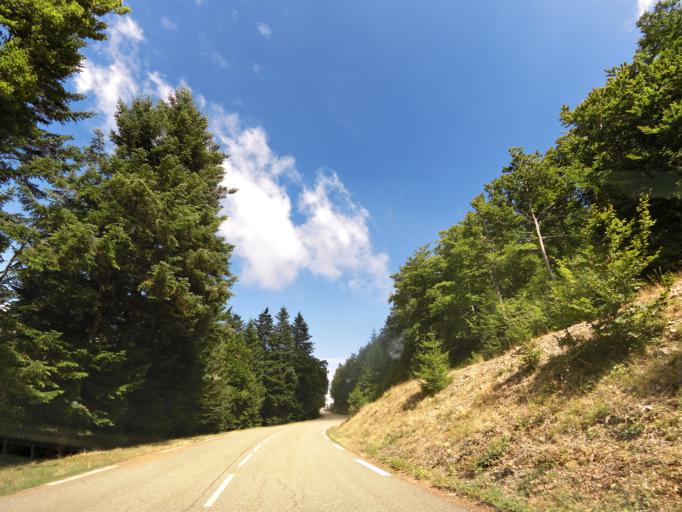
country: FR
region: Languedoc-Roussillon
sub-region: Departement du Gard
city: Valleraugue
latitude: 44.1025
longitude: 3.5377
